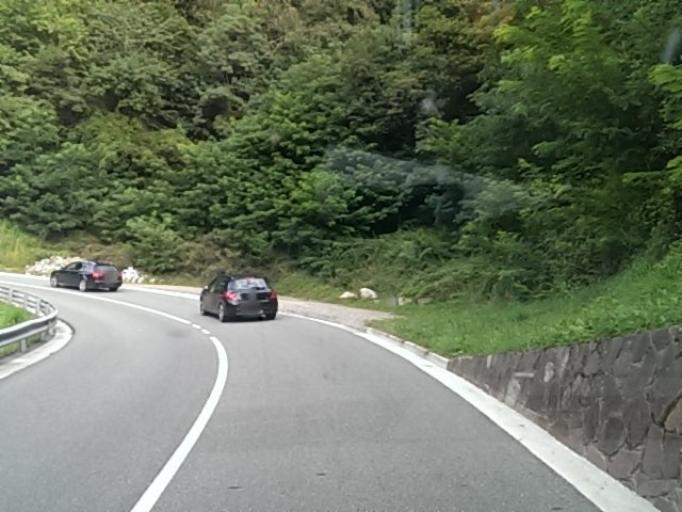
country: IT
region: Trentino-Alto Adige
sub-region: Bolzano
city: San Pancrazio
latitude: 46.6060
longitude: 11.1057
